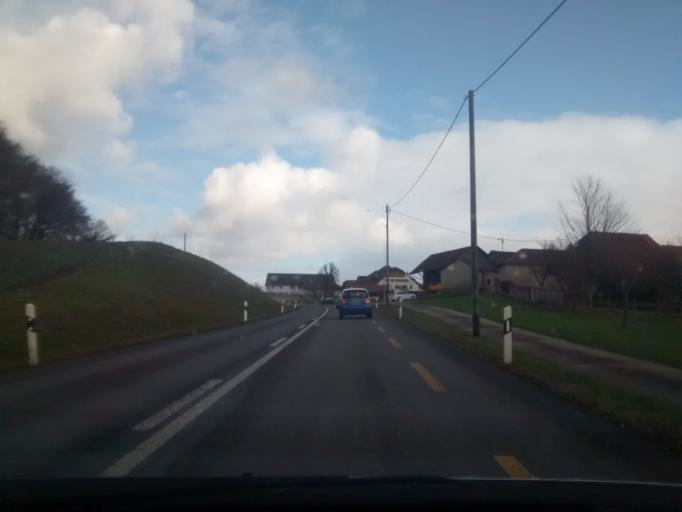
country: CH
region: Vaud
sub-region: Lausanne District
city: Romanel
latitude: 46.5731
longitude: 6.5851
